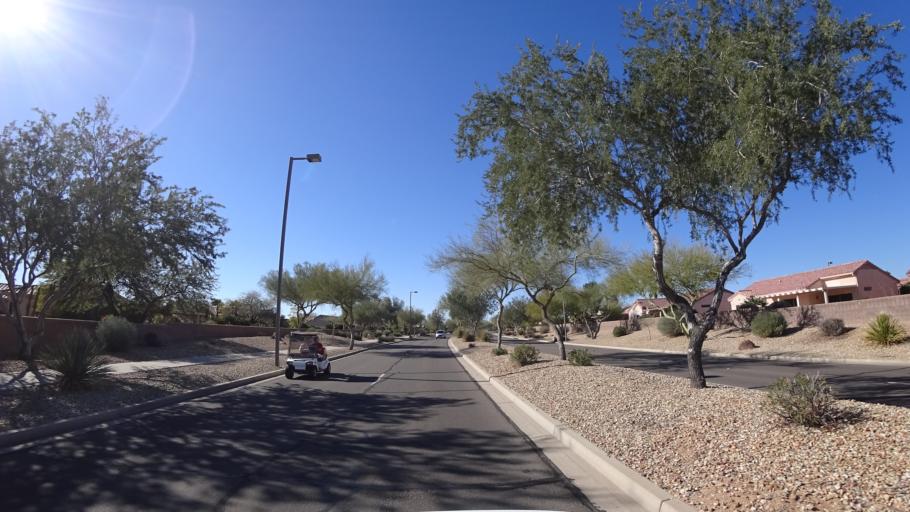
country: US
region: Arizona
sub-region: Maricopa County
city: Sun City West
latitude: 33.6689
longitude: -112.4051
